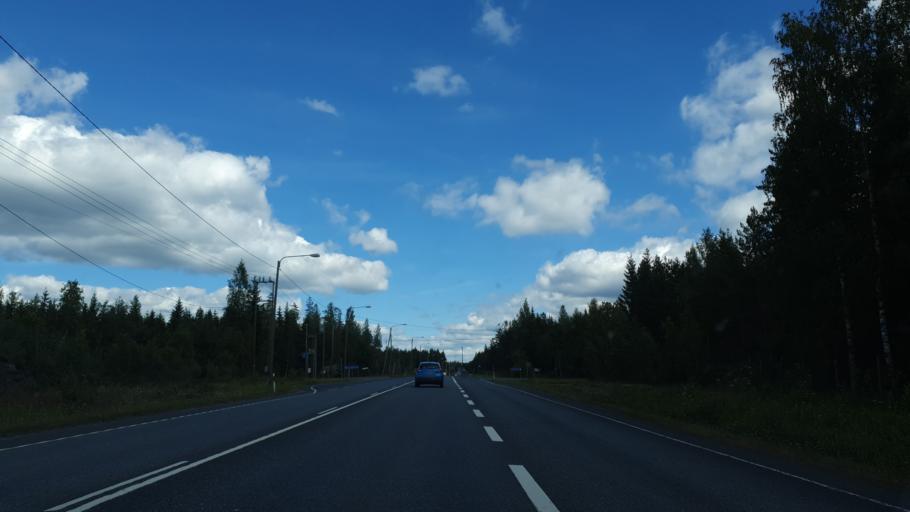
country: FI
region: Pirkanmaa
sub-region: Tampere
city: Orivesi
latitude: 61.6456
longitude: 24.2210
